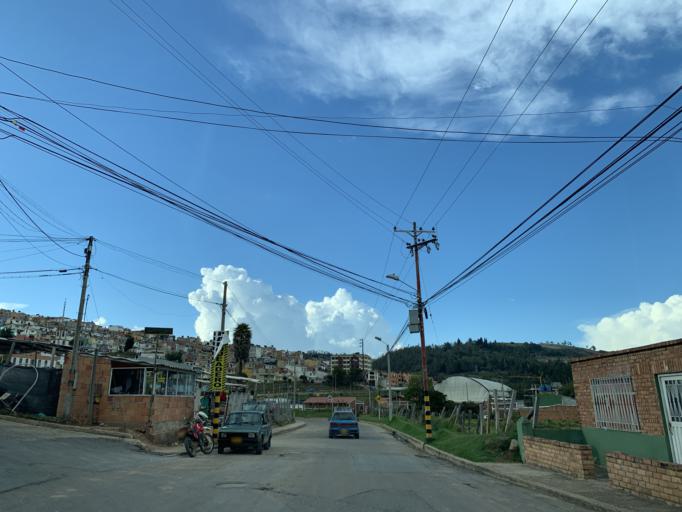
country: CO
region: Boyaca
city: Tunja
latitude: 5.5462
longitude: -73.3602
